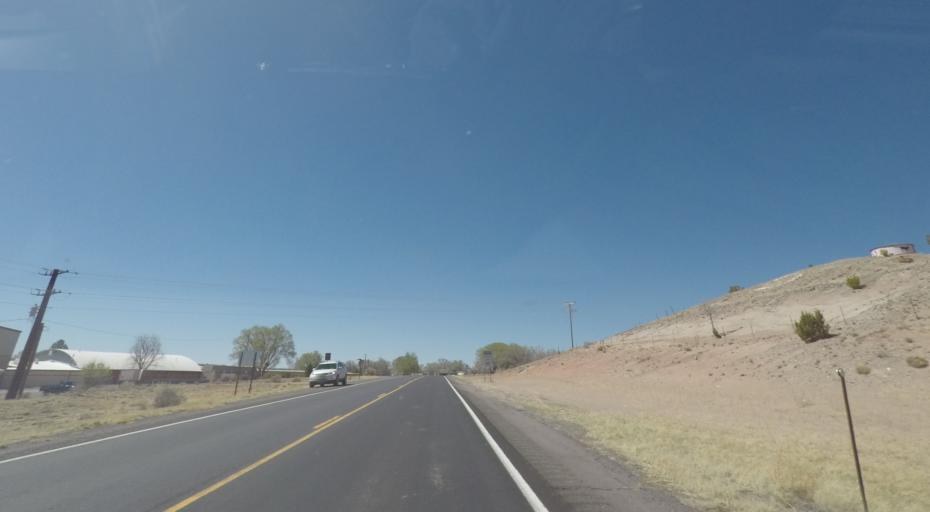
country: US
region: New Mexico
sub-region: Catron County
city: Reserve
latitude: 34.3400
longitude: -108.4904
